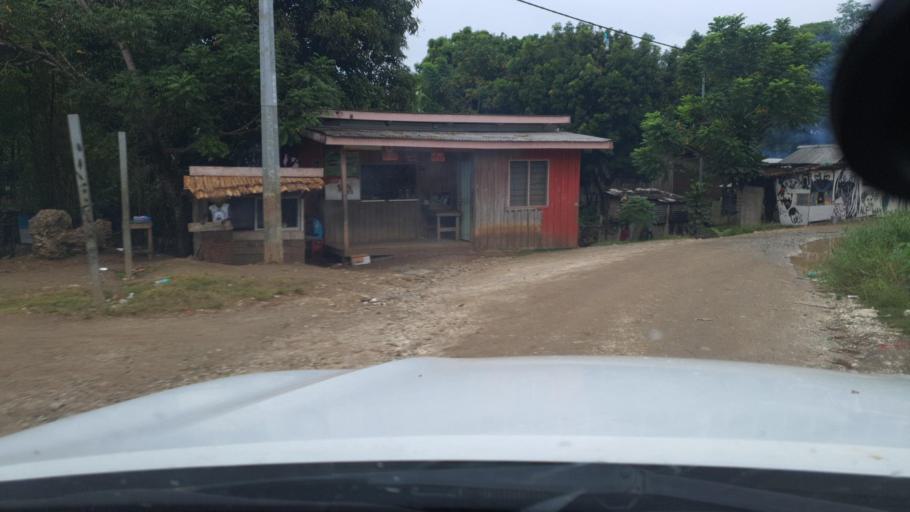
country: SB
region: Guadalcanal
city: Honiara
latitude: -9.4494
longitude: 159.9816
